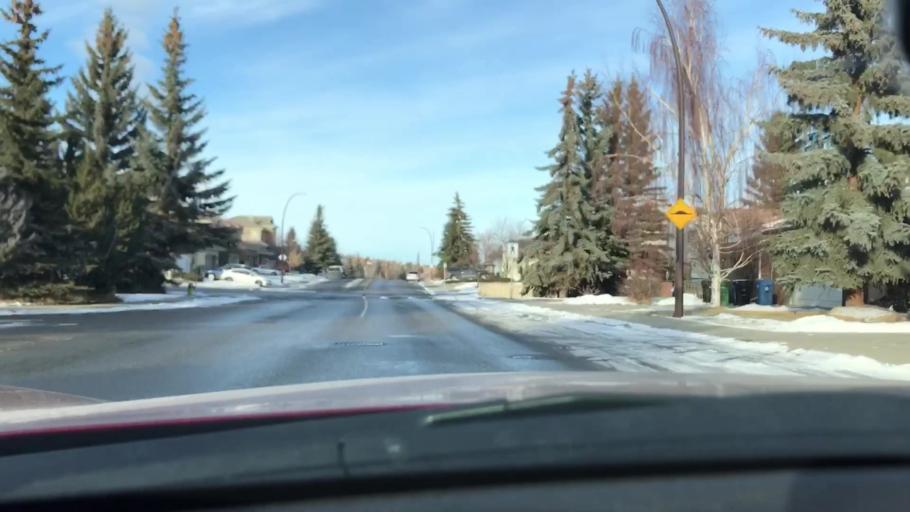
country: CA
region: Alberta
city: Calgary
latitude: 51.0300
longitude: -114.1702
